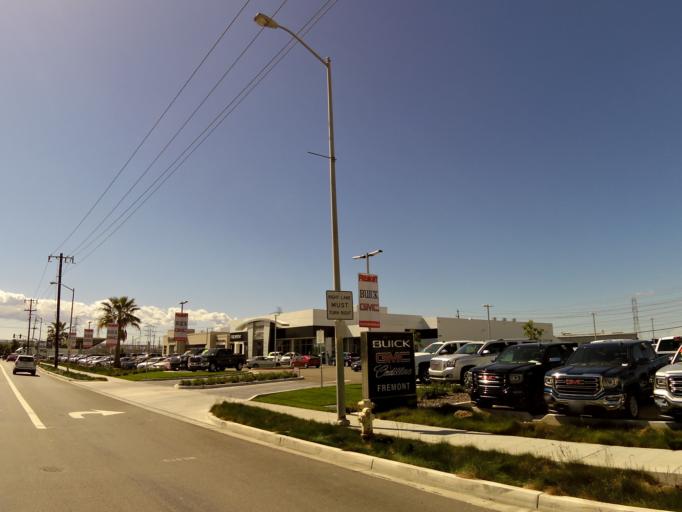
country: US
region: California
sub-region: Alameda County
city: Fremont
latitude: 37.5032
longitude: -121.9778
